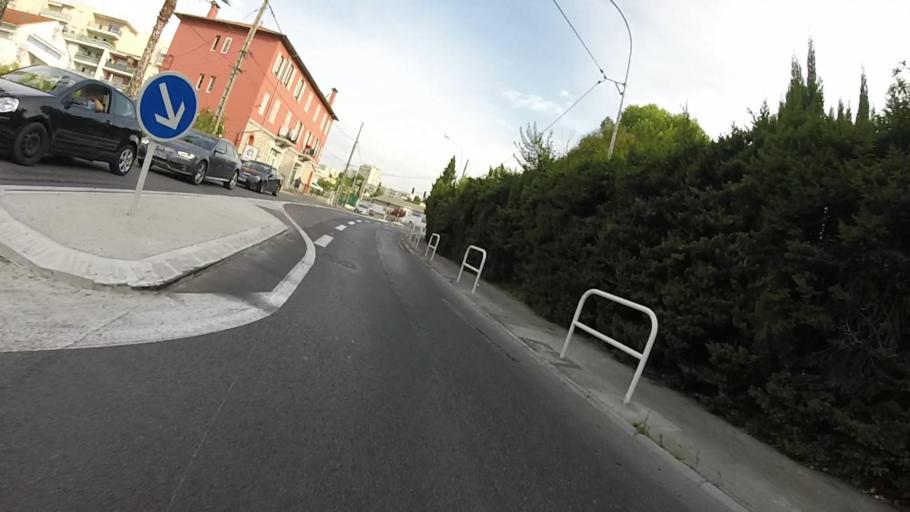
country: FR
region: Provence-Alpes-Cote d'Azur
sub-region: Departement des Alpes-Maritimes
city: Antibes
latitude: 43.5907
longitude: 7.1063
